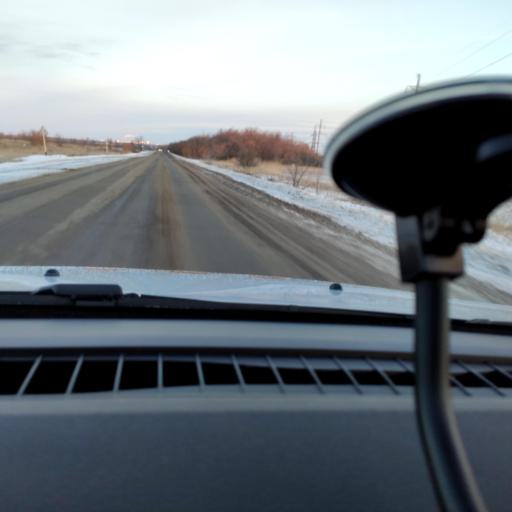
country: RU
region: Samara
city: Dubovyy Umet
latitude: 53.0865
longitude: 50.2346
